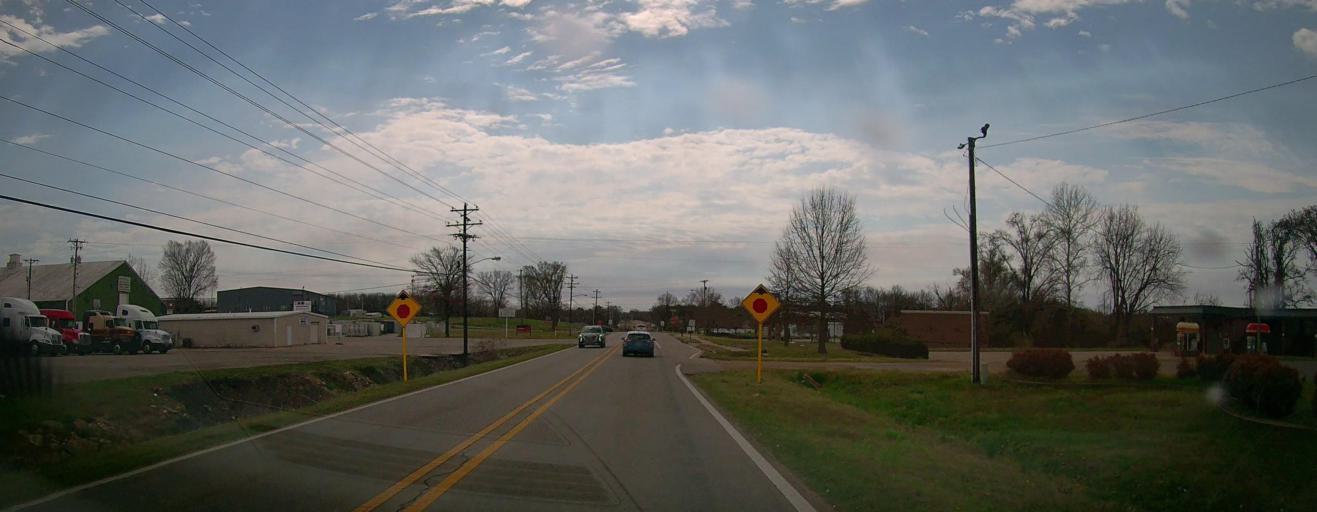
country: US
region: Mississippi
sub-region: De Soto County
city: Olive Branch
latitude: 34.9506
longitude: -89.8125
